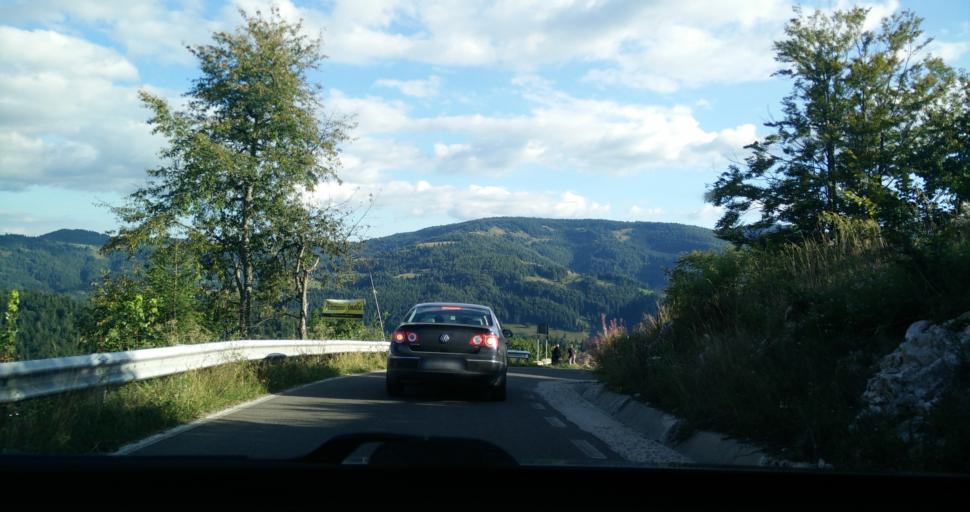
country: RO
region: Alba
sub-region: Comuna Scarisoara
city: Scarisoara
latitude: 46.4693
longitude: 22.8324
